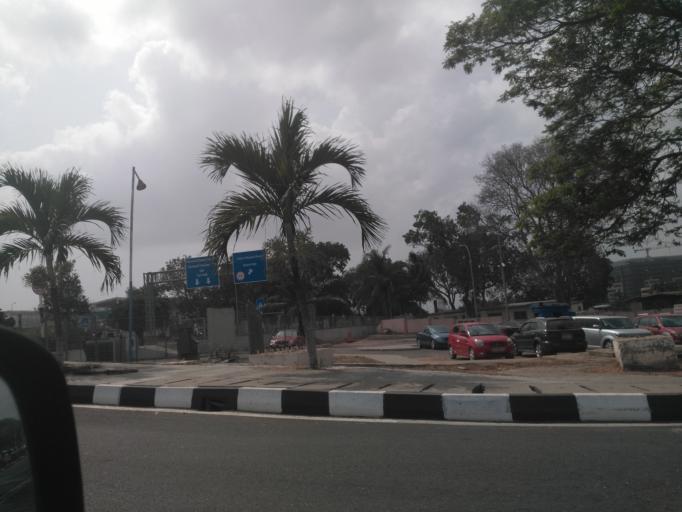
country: GH
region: Greater Accra
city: Accra
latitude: 5.6054
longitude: -0.1733
